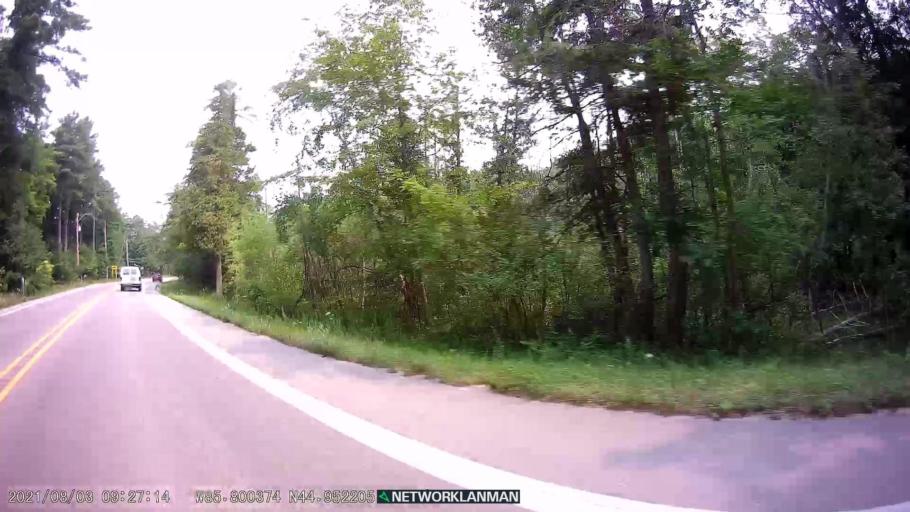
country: US
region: Michigan
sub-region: Leelanau County
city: Leland
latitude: 44.9524
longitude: -85.8004
